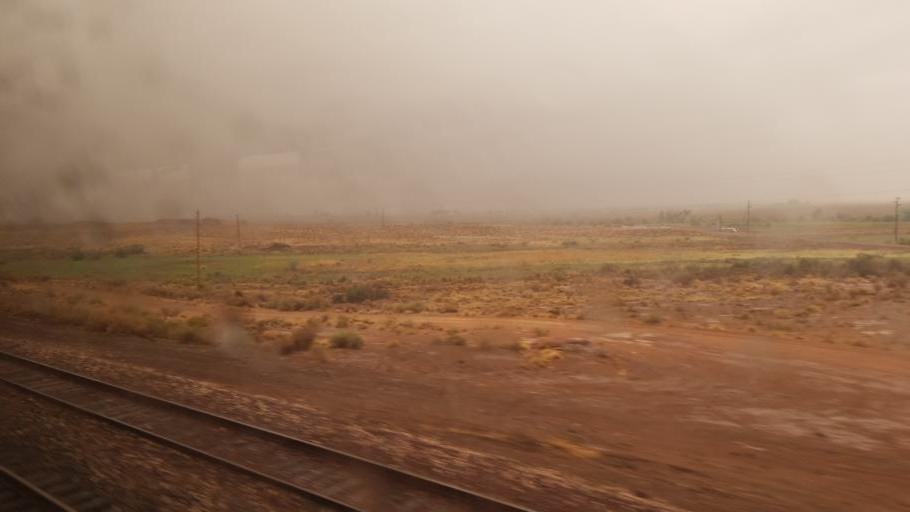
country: US
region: Arizona
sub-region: Navajo County
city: Joseph City
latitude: 34.9082
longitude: -110.2602
